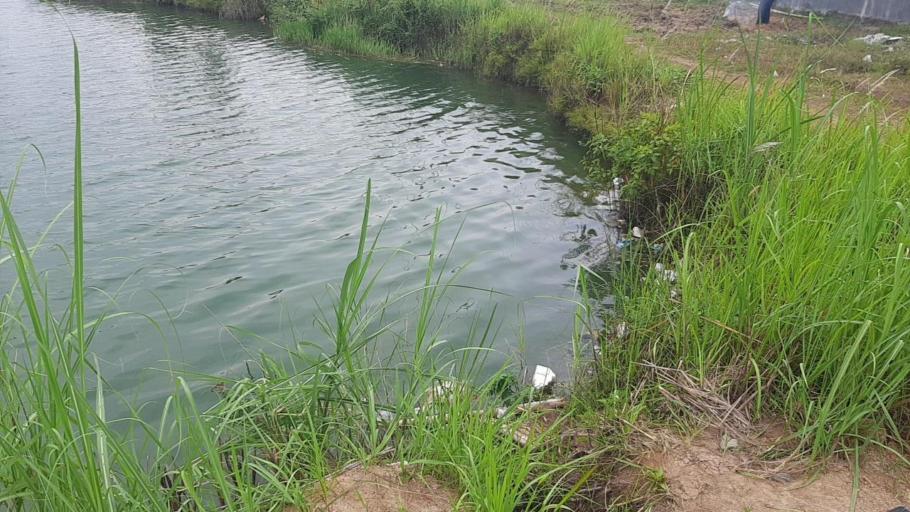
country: ID
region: West Java
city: Cileungsir
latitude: -6.4424
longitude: 107.0244
